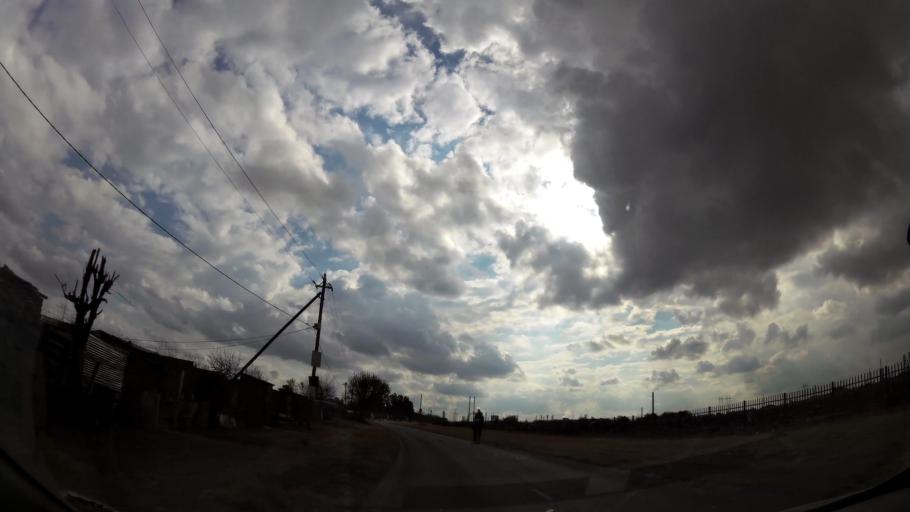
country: ZA
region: Orange Free State
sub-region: Fezile Dabi District Municipality
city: Sasolburg
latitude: -26.8389
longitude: 27.8612
